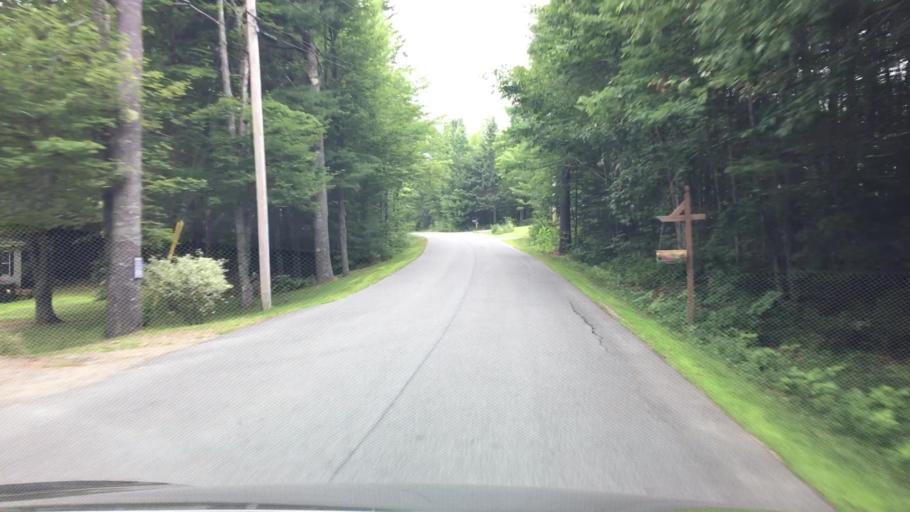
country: US
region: Maine
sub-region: Waldo County
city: Stockton Springs
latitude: 44.5179
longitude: -68.8766
